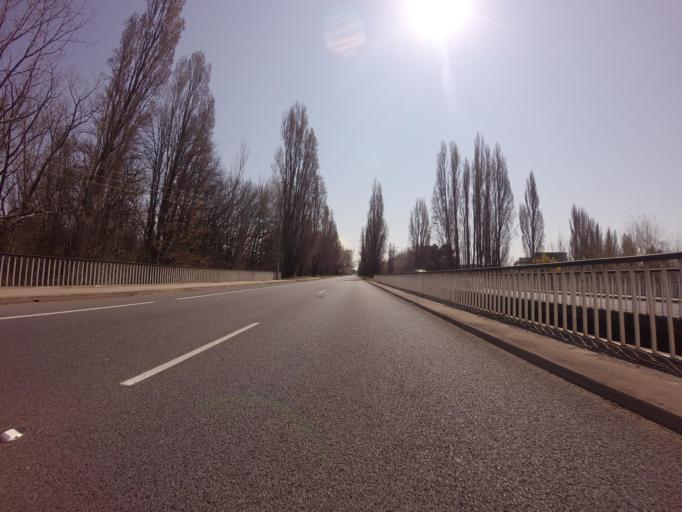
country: AU
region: Australian Capital Territory
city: Forrest
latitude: -35.3292
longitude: 149.1594
